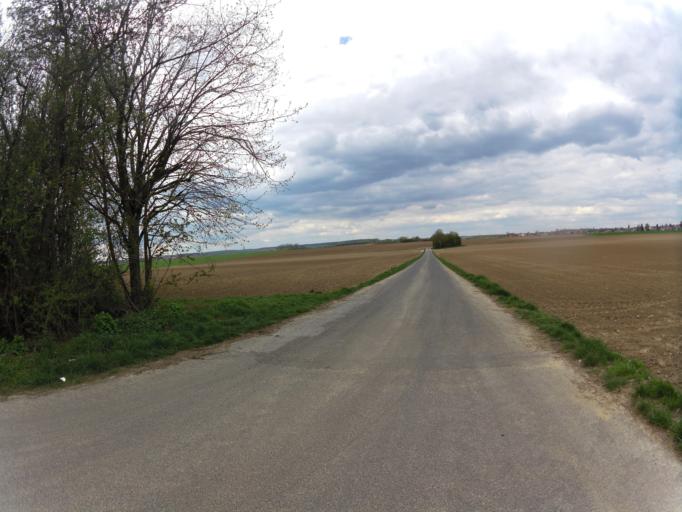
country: DE
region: Bavaria
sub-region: Regierungsbezirk Unterfranken
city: Giebelstadt
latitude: 49.6434
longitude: 9.9362
